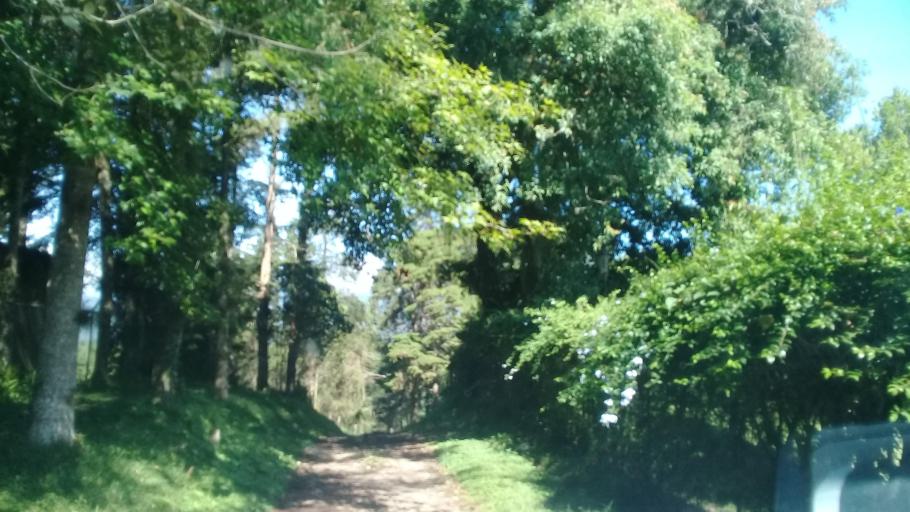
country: MX
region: Veracruz
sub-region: Tlalnelhuayocan
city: Guadalupe Victoria
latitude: 19.5343
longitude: -96.9501
